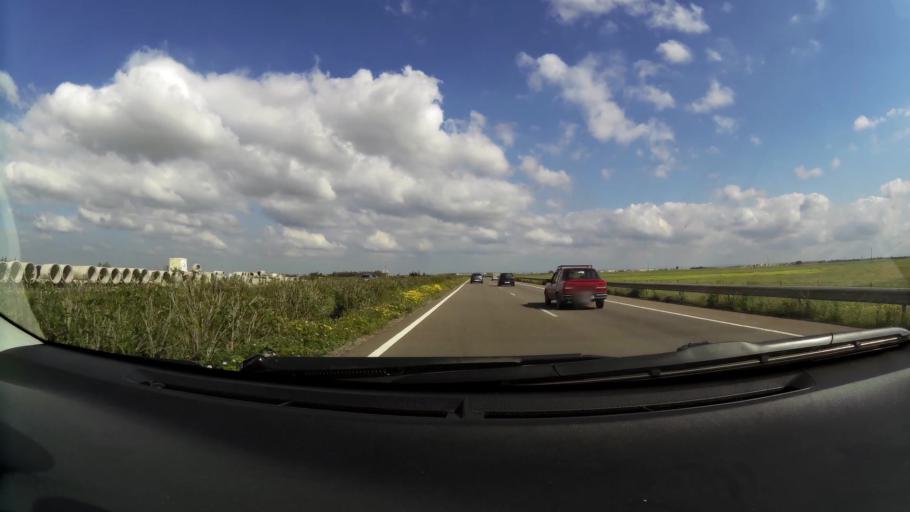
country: MA
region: Chaouia-Ouardigha
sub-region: Settat Province
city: Berrechid
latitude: 33.3115
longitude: -7.5934
